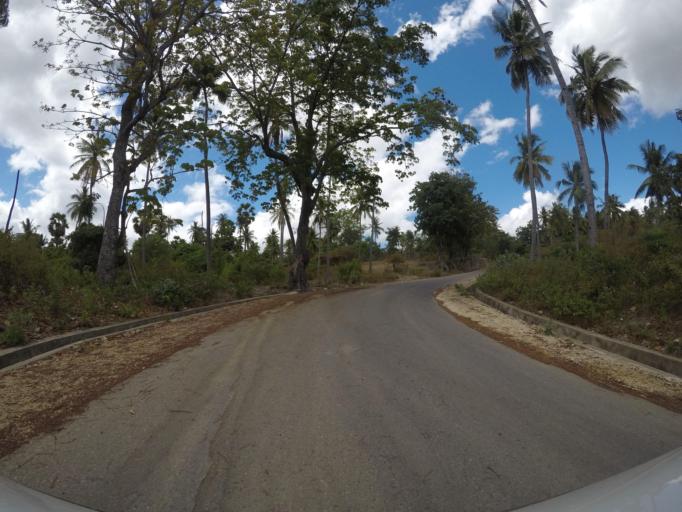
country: TL
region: Lautem
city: Lospalos
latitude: -8.3552
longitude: 126.9305
